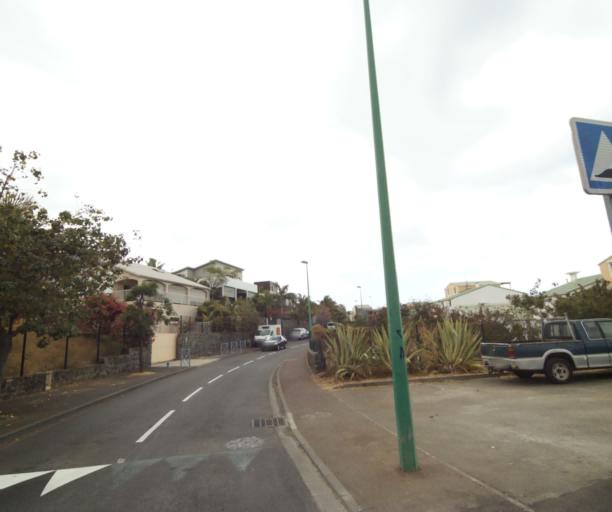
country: RE
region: Reunion
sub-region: Reunion
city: Saint-Paul
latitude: -21.0630
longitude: 55.2294
